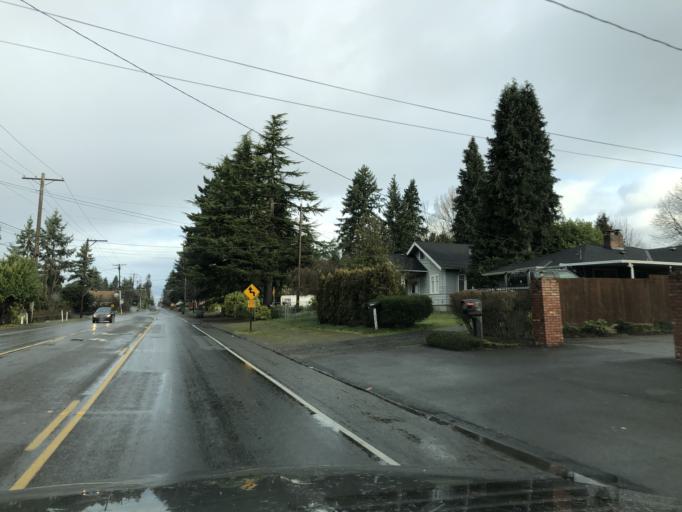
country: US
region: Washington
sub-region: Pierce County
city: Parkland
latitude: 47.1668
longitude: -122.4420
